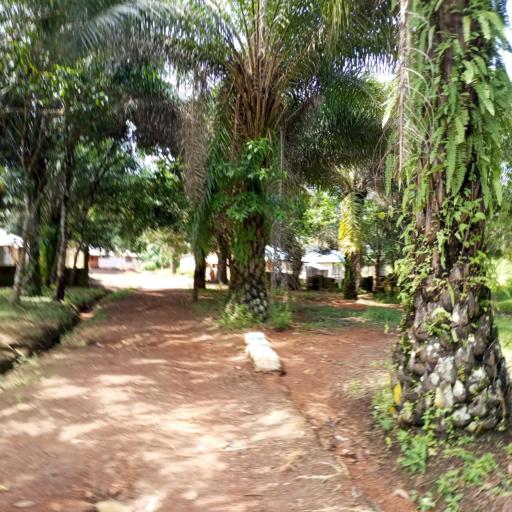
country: SL
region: Northern Province
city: Kambia
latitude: 9.1188
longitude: -12.9148
